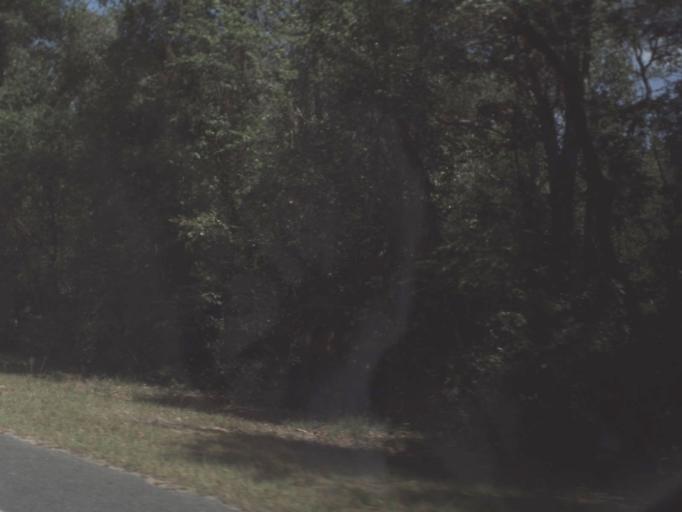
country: US
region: Florida
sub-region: Marion County
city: Ocala
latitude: 29.2194
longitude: -82.0381
